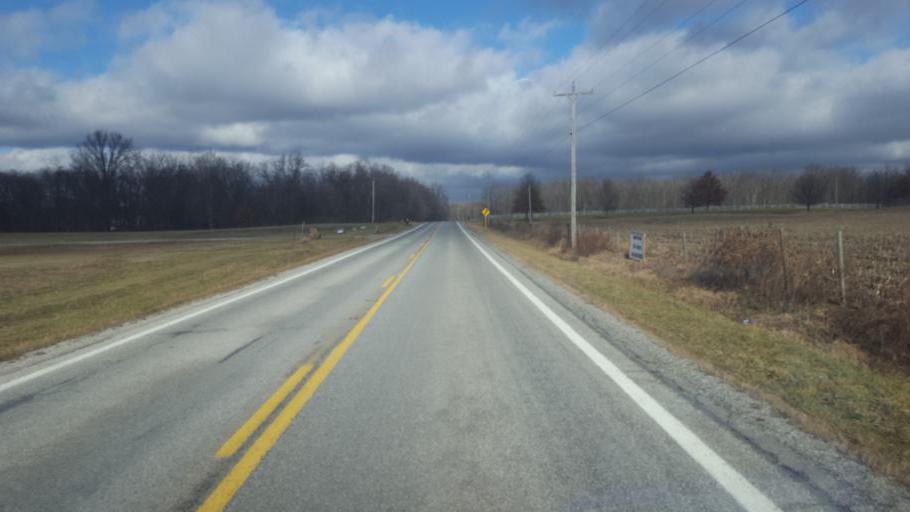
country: US
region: Ohio
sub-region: Morrow County
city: Mount Gilead
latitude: 40.4957
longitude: -82.8199
